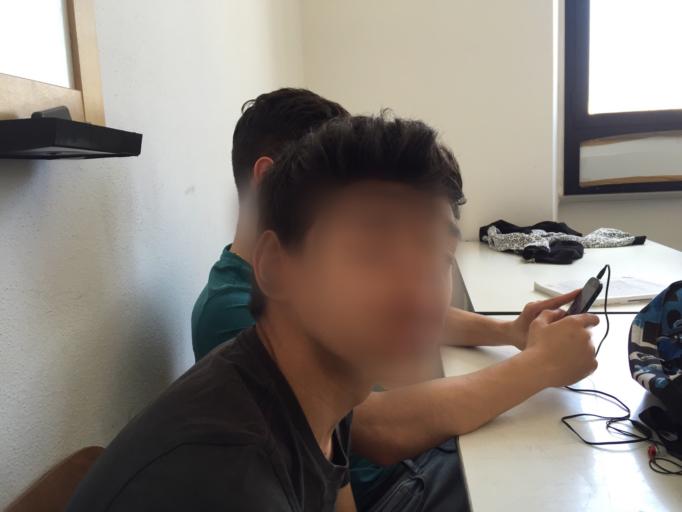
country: IT
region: Sardinia
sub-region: Provincia di Cagliari
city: Cagliari
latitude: 39.2149
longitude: 9.1225
